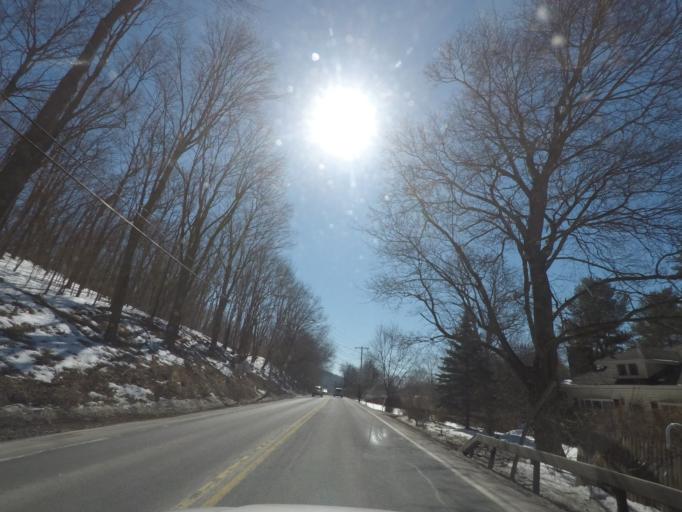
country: US
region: New York
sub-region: Saratoga County
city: Waterford
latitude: 42.8391
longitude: -73.6247
